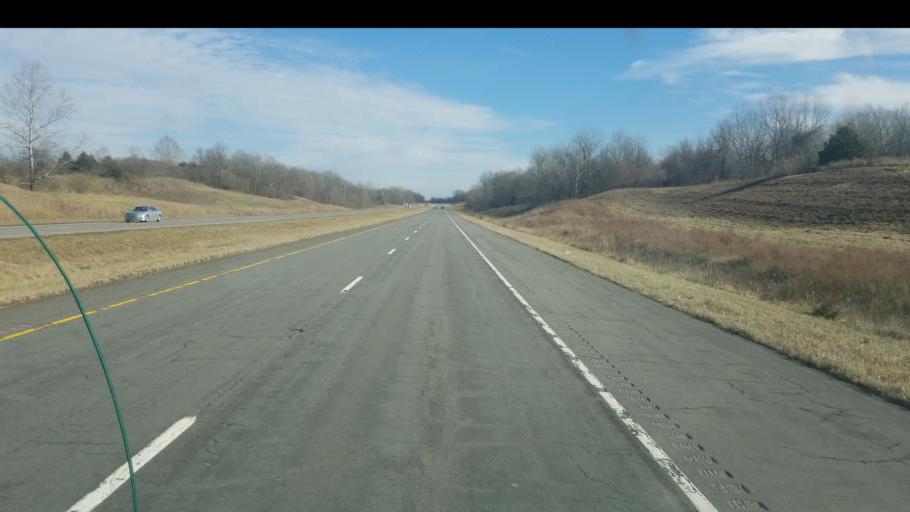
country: US
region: Illinois
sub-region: Saline County
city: Carrier Mills
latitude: 37.7303
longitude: -88.7596
